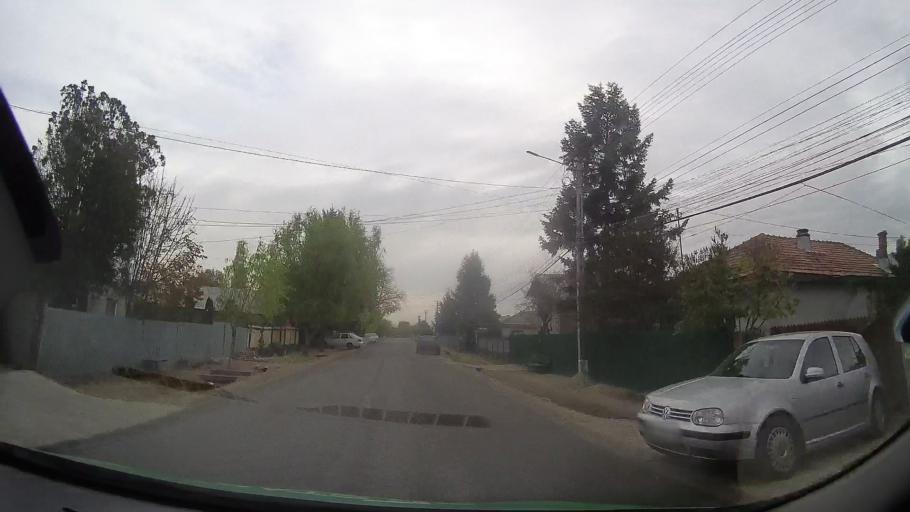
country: RO
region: Prahova
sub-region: Comuna Valea Calugareasca
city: Pantazi
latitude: 44.9357
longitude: 26.1388
